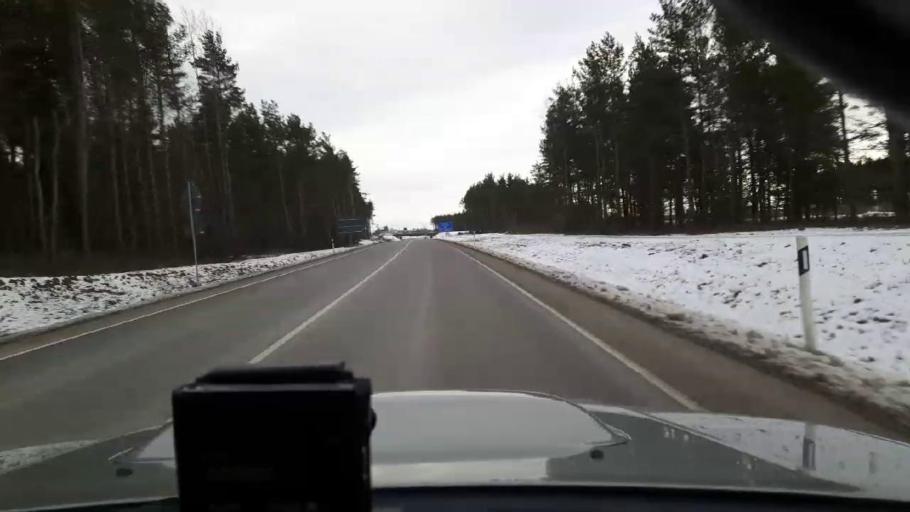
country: EE
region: Harju
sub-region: Saue vald
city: Laagri
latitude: 59.3450
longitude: 24.6020
